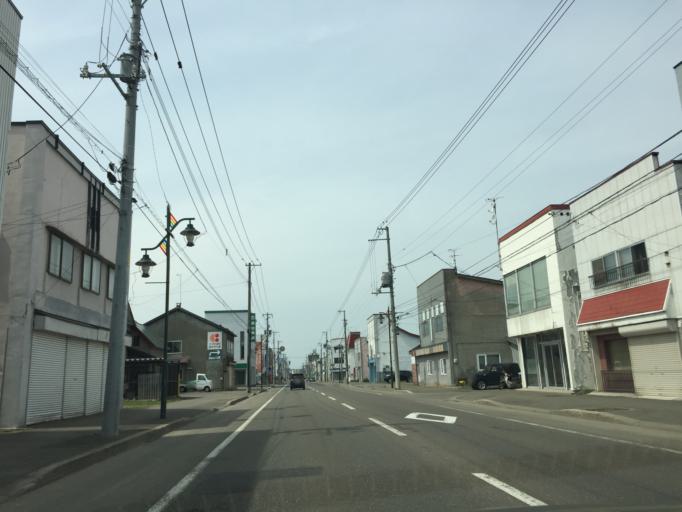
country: JP
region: Hokkaido
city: Akabira
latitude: 43.5530
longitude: 142.0537
